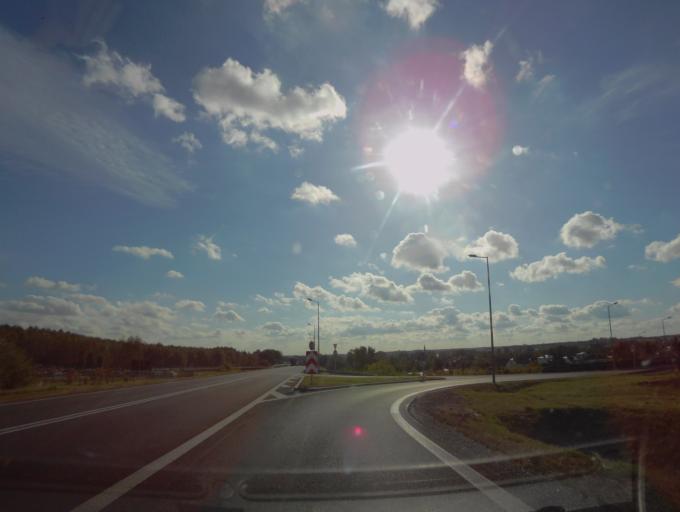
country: PL
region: Subcarpathian Voivodeship
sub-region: Powiat lezajski
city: Giedlarowa
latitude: 50.2418
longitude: 22.4112
